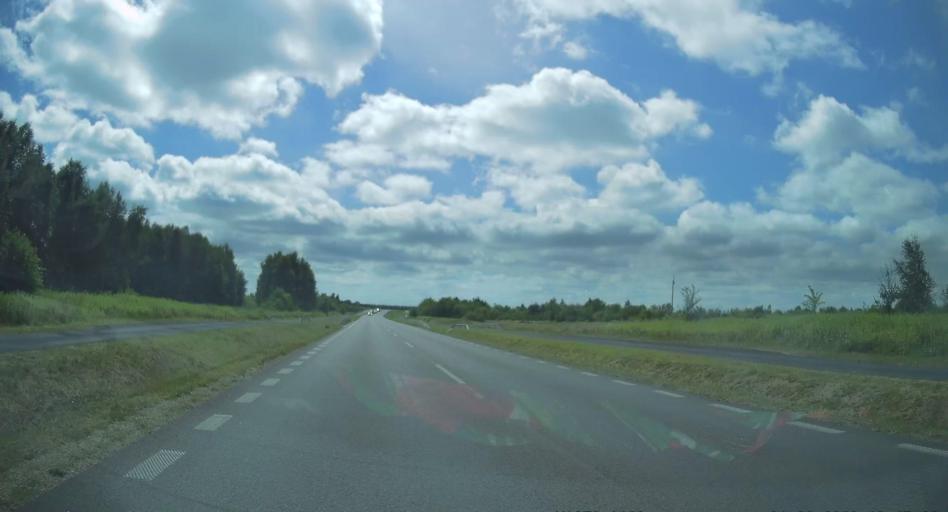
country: PL
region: Subcarpathian Voivodeship
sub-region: Powiat mielecki
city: Mielec
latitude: 50.3456
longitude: 21.4943
